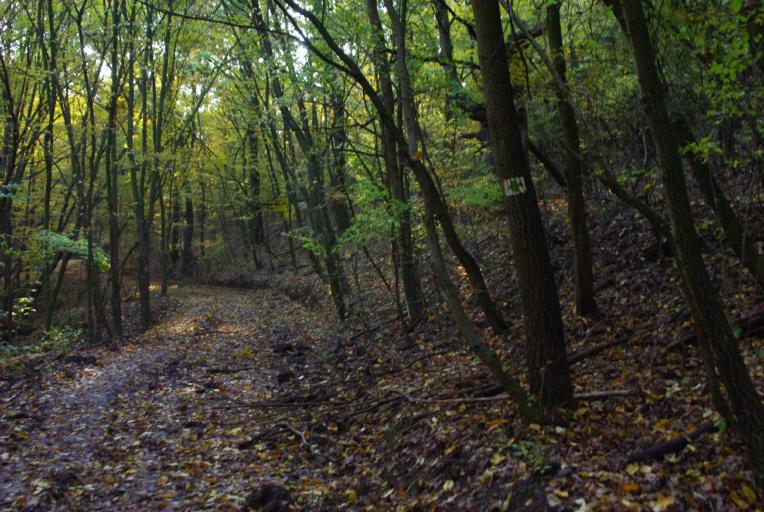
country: HU
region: Pest
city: Nagymaros
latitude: 47.8179
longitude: 18.9360
